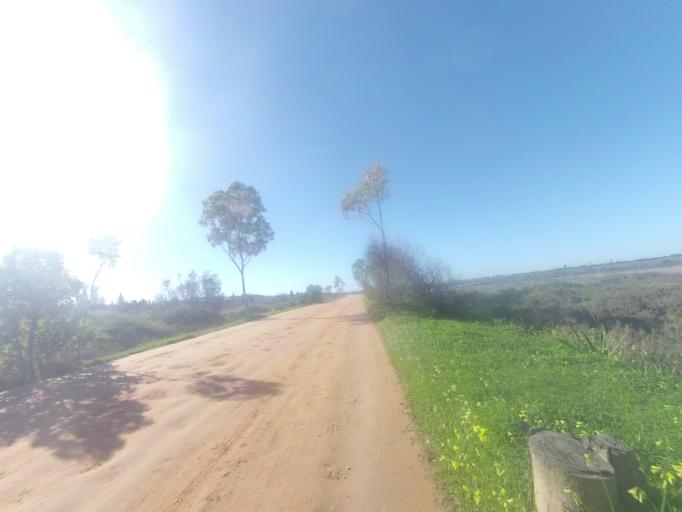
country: ES
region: Andalusia
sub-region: Provincia de Huelva
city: Palos de la Frontera
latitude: 37.2294
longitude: -6.9067
